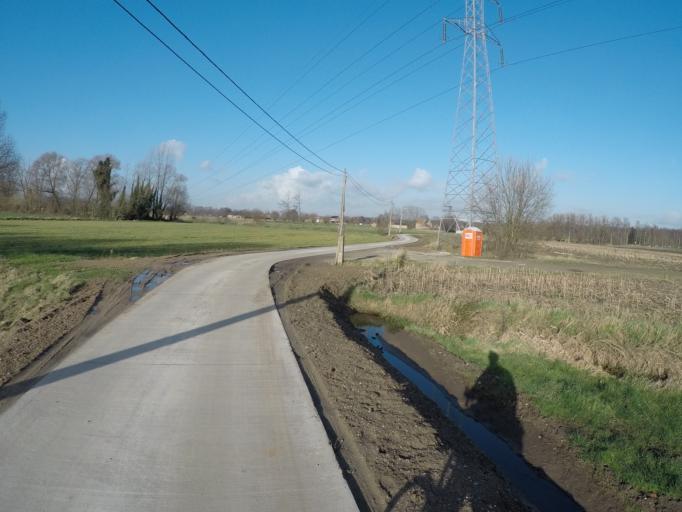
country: BE
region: Flanders
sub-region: Provincie Antwerpen
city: Ranst
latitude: 51.2101
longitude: 4.5726
